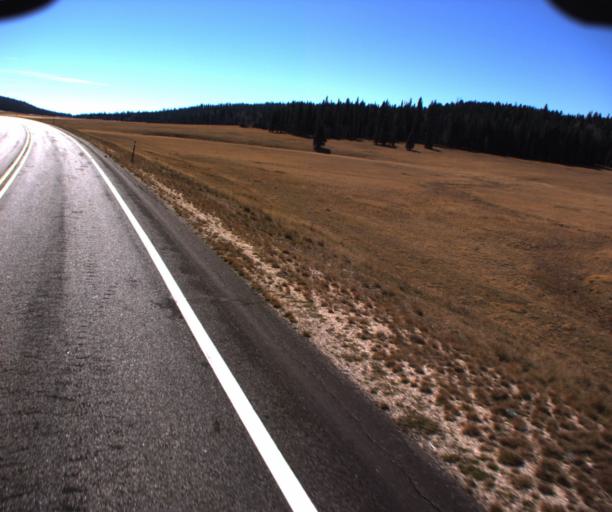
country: US
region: Arizona
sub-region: Coconino County
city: Grand Canyon
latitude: 36.3774
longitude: -112.1258
